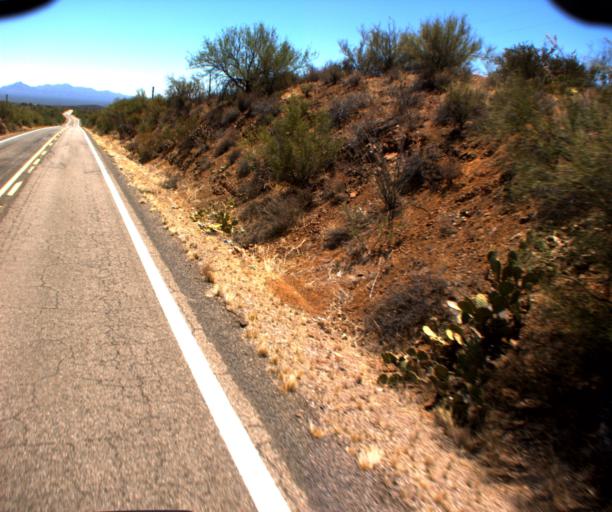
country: US
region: Arizona
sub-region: Pima County
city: Sells
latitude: 32.1699
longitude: -112.1445
